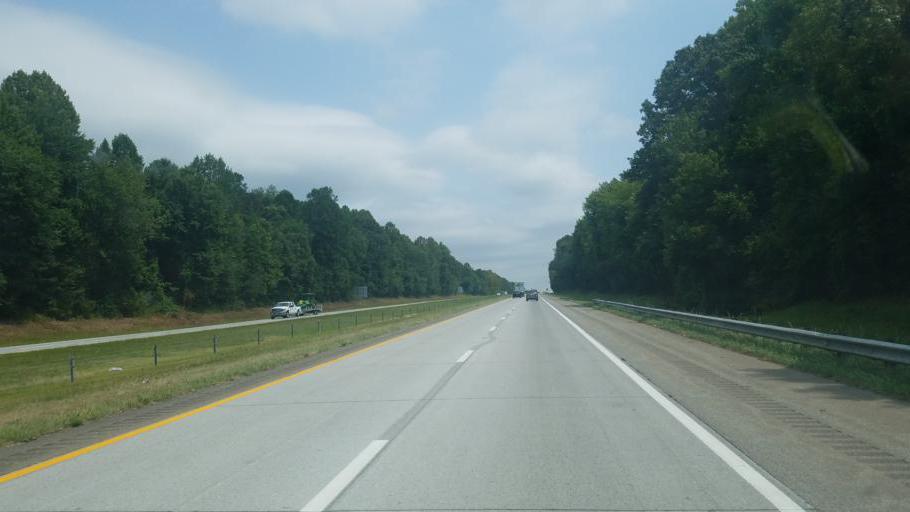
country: US
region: North Carolina
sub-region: Surry County
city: Elkin
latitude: 36.2920
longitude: -80.8148
